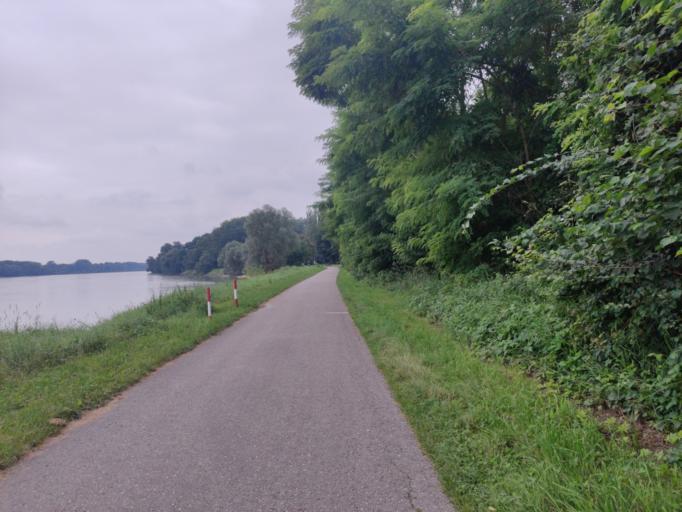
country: AT
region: Lower Austria
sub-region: Politischer Bezirk Tulln
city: Atzenbrugg
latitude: 48.3480
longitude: 15.9093
